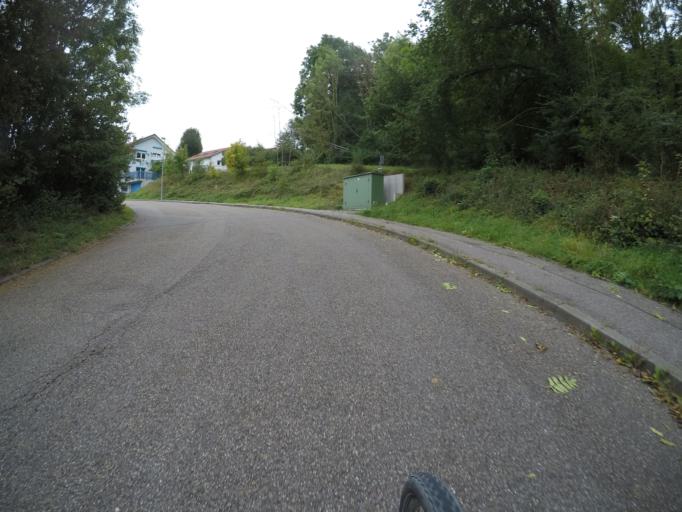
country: DE
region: Baden-Wuerttemberg
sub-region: Regierungsbezirk Stuttgart
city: Eberdingen
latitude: 48.8910
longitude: 8.9676
